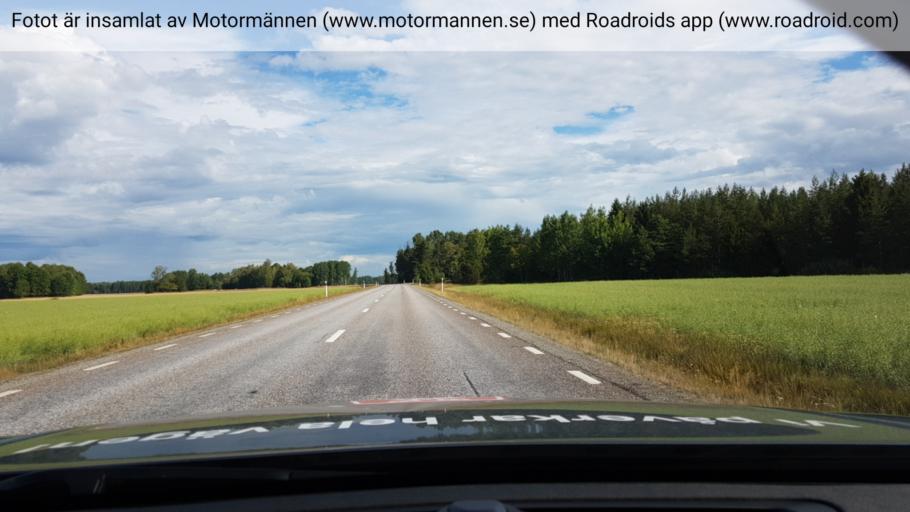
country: SE
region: Uppsala
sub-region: Enkopings Kommun
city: Irsta
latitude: 59.7813
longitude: 16.9067
